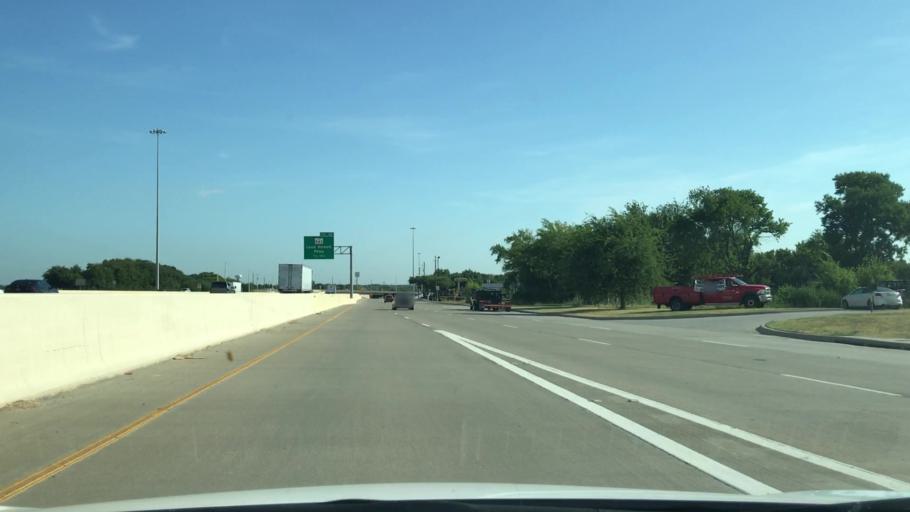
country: US
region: Texas
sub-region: Collin County
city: McKinney
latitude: 33.2340
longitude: -96.6313
